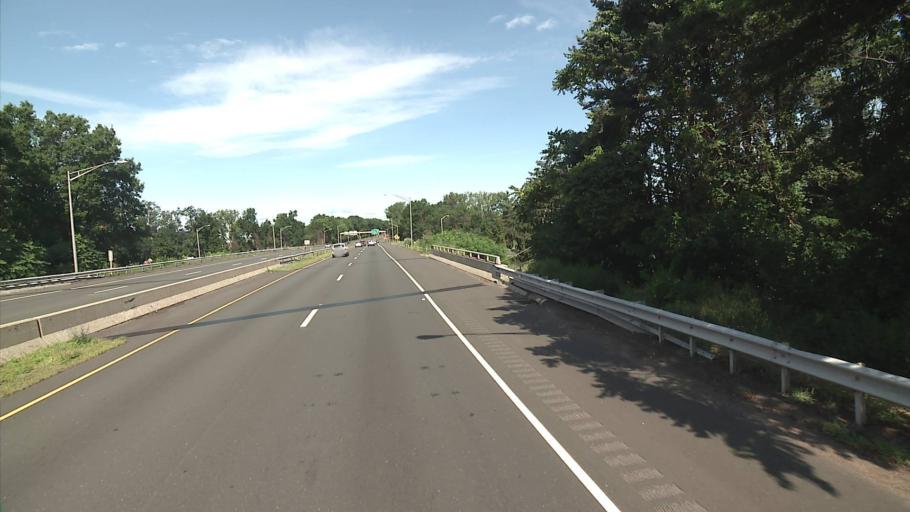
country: US
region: Connecticut
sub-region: Hartford County
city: Wethersfield
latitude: 41.7416
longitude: -72.6338
